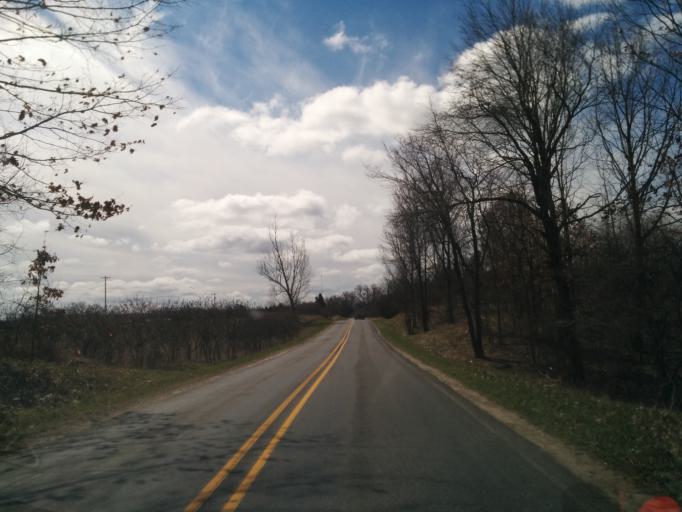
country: US
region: Michigan
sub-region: Newaygo County
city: Newaygo
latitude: 43.4215
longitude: -85.6423
